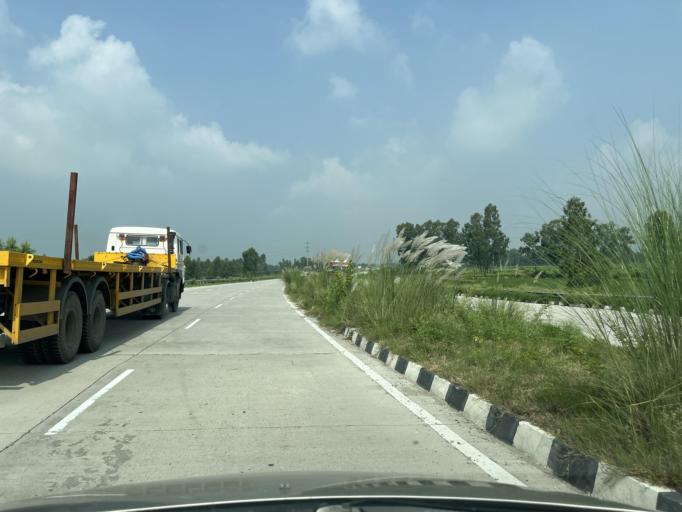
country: IN
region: Uttarakhand
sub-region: Udham Singh Nagar
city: Kashipur
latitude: 29.1637
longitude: 78.9622
